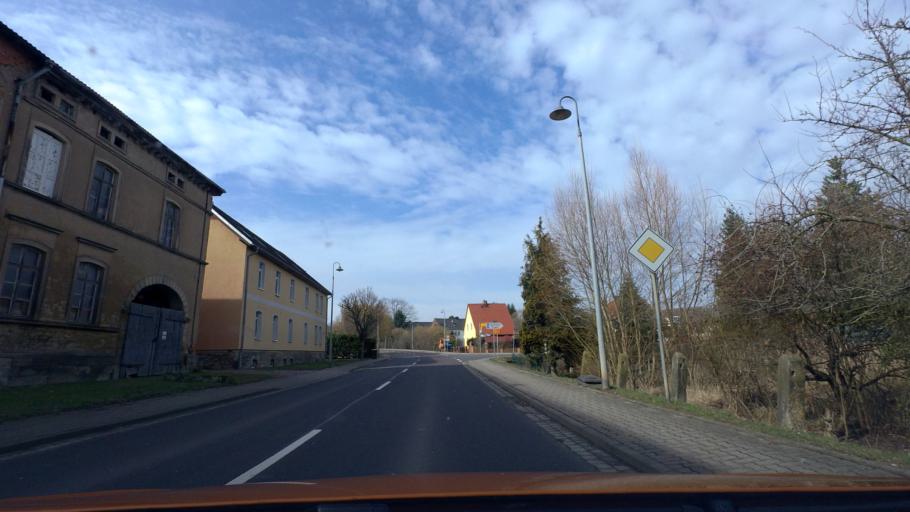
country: DE
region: Saxony-Anhalt
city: Beendorf
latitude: 52.2194
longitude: 11.1088
